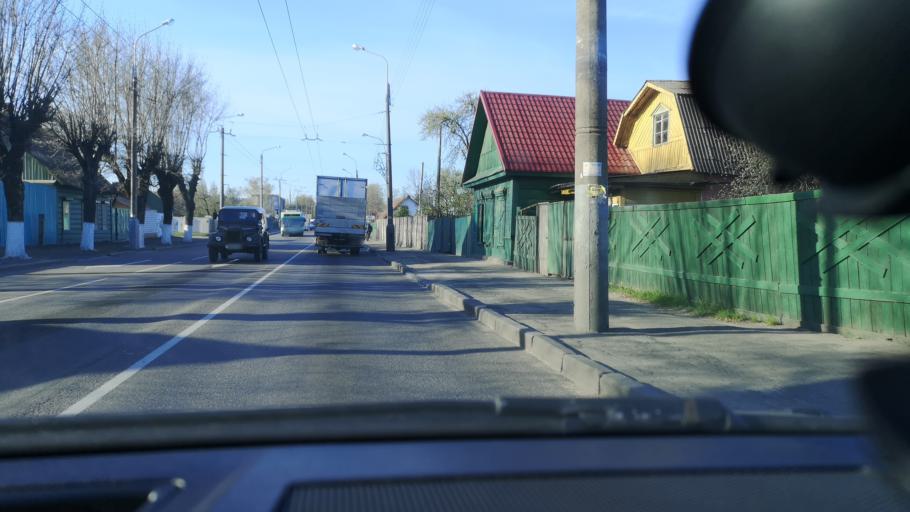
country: BY
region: Gomel
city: Gomel
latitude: 52.4255
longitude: 30.9740
